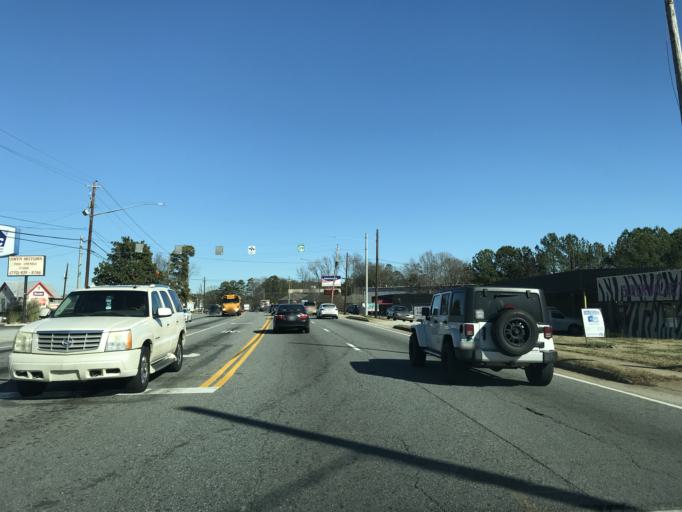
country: US
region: Georgia
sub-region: DeKalb County
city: Tucker
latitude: 33.8378
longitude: -84.2375
